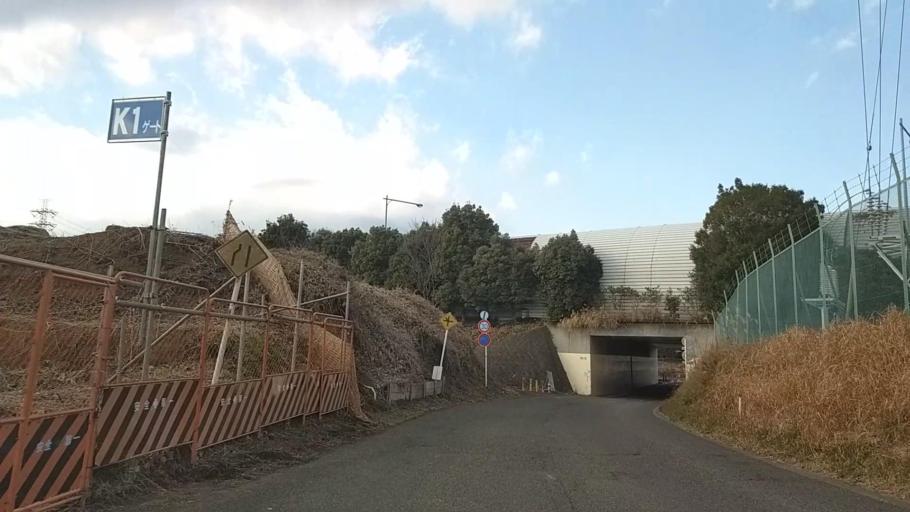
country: JP
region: Kanagawa
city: Isehara
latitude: 35.4126
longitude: 139.3169
